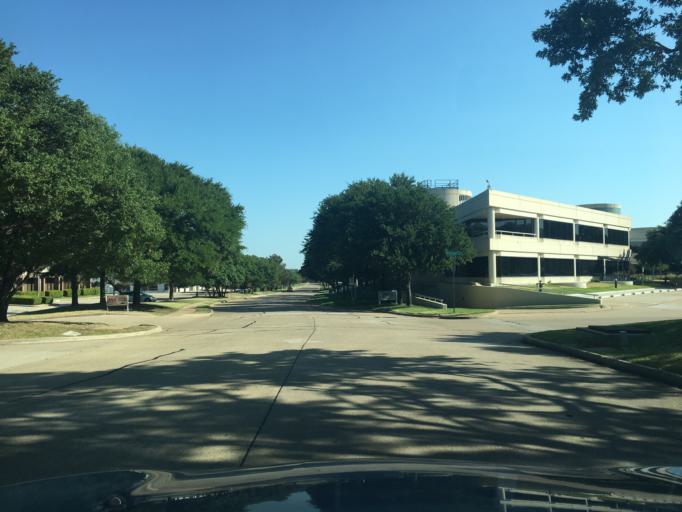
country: US
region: Texas
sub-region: Dallas County
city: Addison
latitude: 32.9634
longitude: -96.8448
